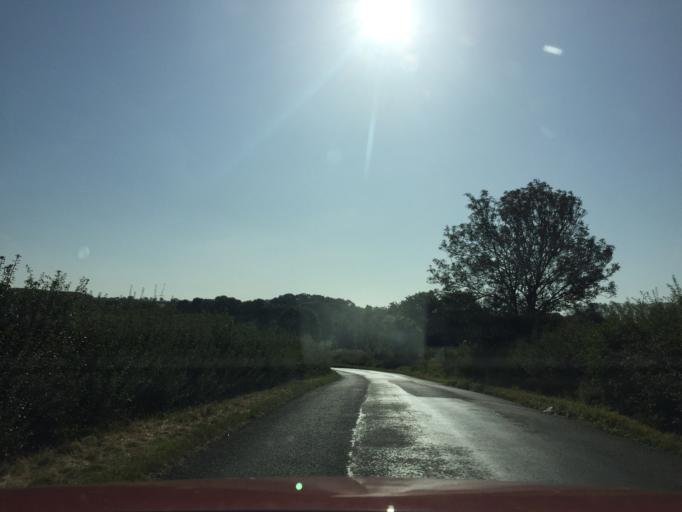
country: GB
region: England
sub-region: Leicestershire
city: Houghton on the Hill
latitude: 52.6466
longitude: -0.9842
